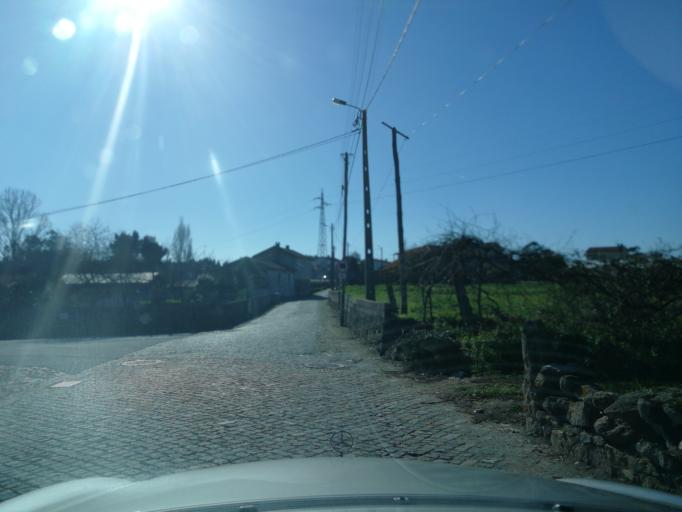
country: PT
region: Porto
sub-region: Vila do Conde
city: Vila do Conde
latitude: 41.3703
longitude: -8.7337
